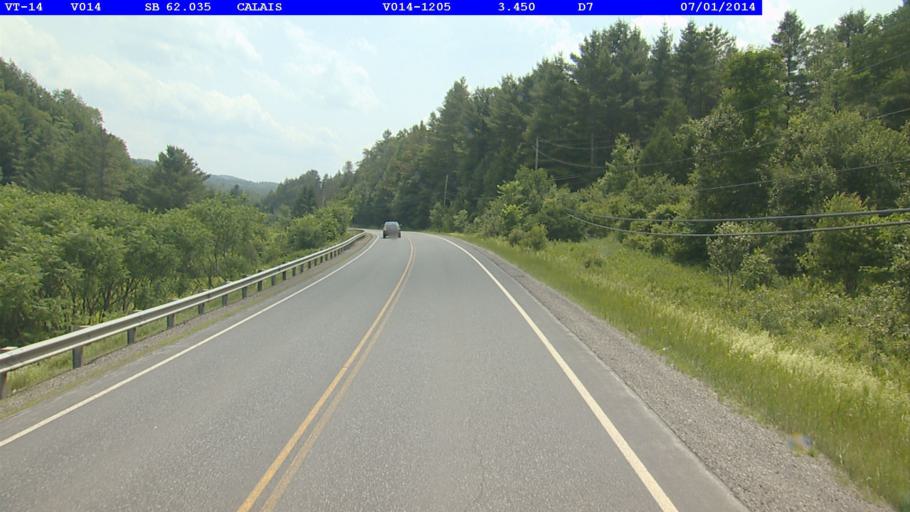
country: US
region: Vermont
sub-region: Washington County
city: Montpelier
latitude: 44.3554
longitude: -72.4452
